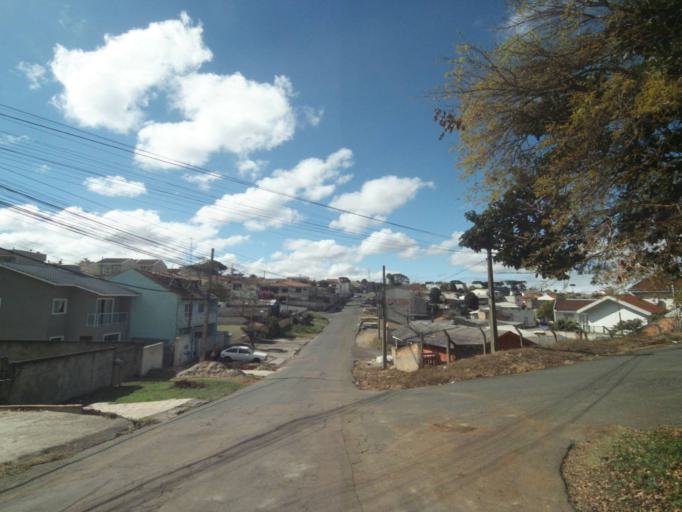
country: BR
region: Parana
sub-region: Sao Jose Dos Pinhais
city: Sao Jose dos Pinhais
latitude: -25.5333
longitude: -49.2903
